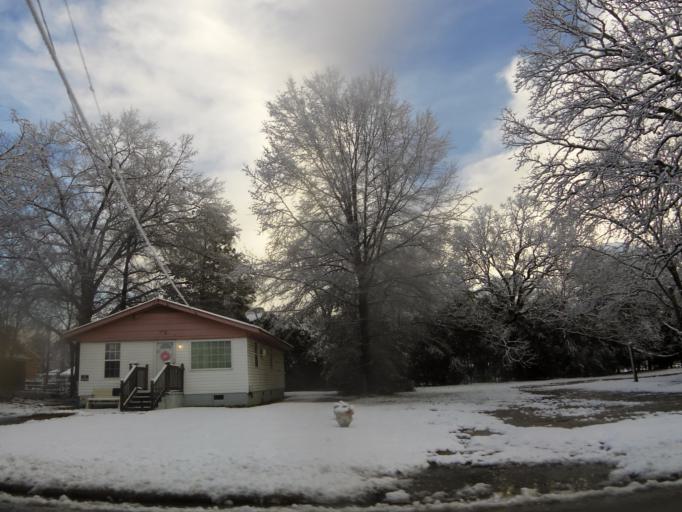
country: US
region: North Carolina
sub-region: Nash County
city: Rocky Mount
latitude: 35.9281
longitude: -77.8147
